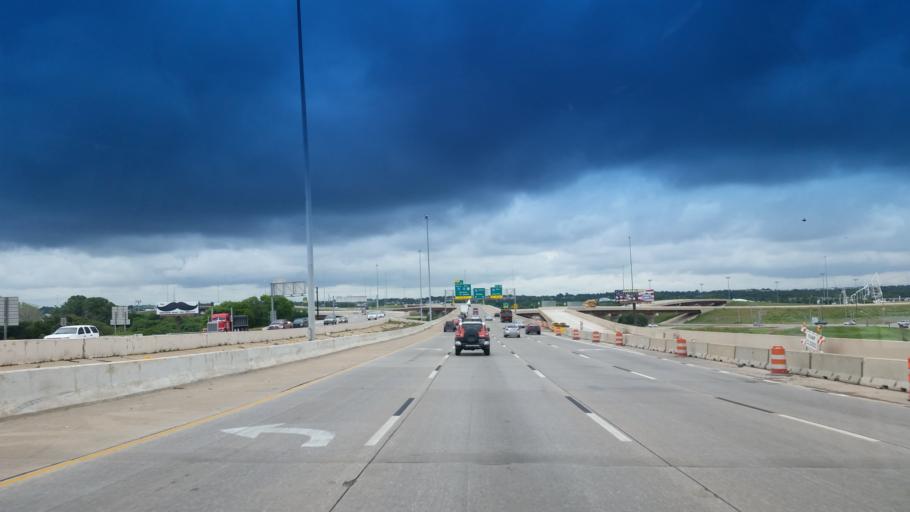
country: US
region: Oklahoma
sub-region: Oklahoma County
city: Oklahoma City
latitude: 35.4676
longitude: -97.5016
